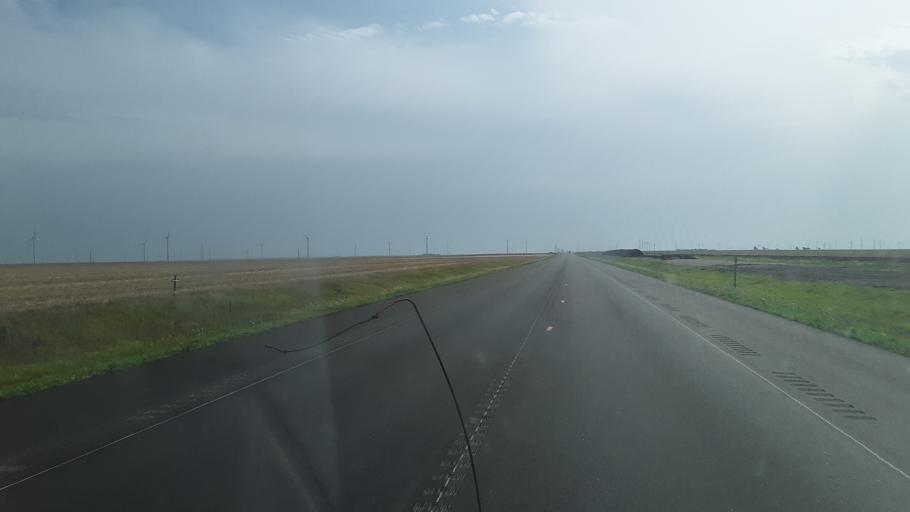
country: US
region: Kansas
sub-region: Ford County
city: Dodge City
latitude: 37.7886
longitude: -99.8804
